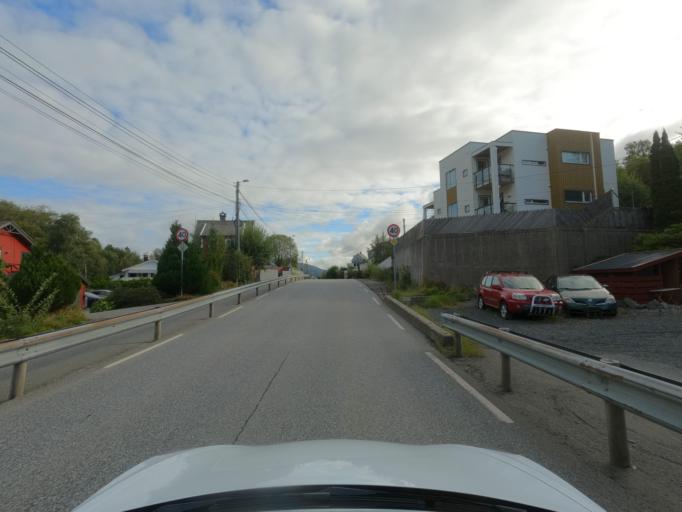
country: NO
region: Hordaland
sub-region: Bergen
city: Sandsli
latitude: 60.3054
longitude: 5.3500
